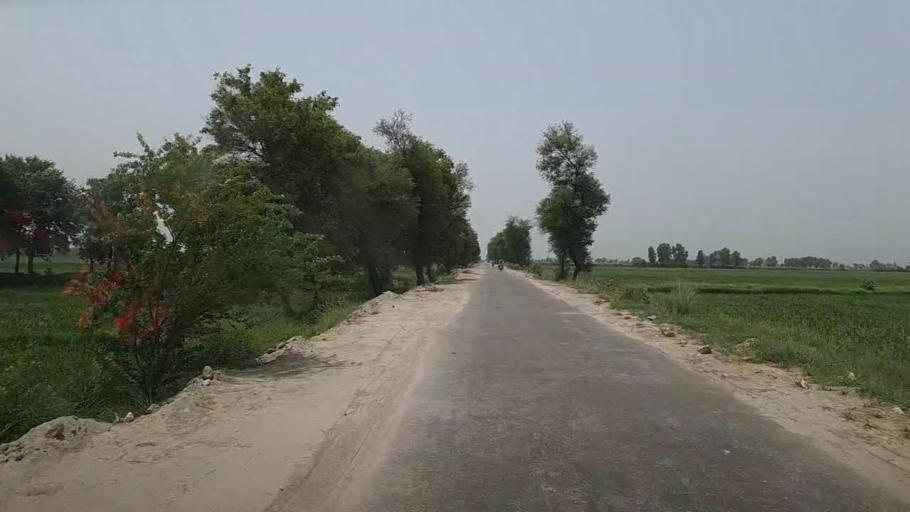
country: PK
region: Sindh
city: Sita Road
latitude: 27.0746
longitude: 67.9077
